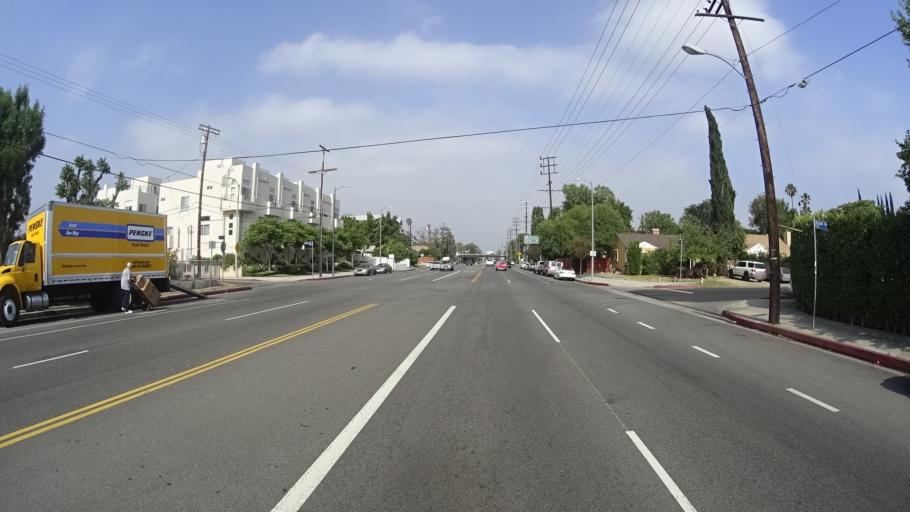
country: US
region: California
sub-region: Los Angeles County
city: North Hollywood
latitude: 34.1721
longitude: -118.3924
